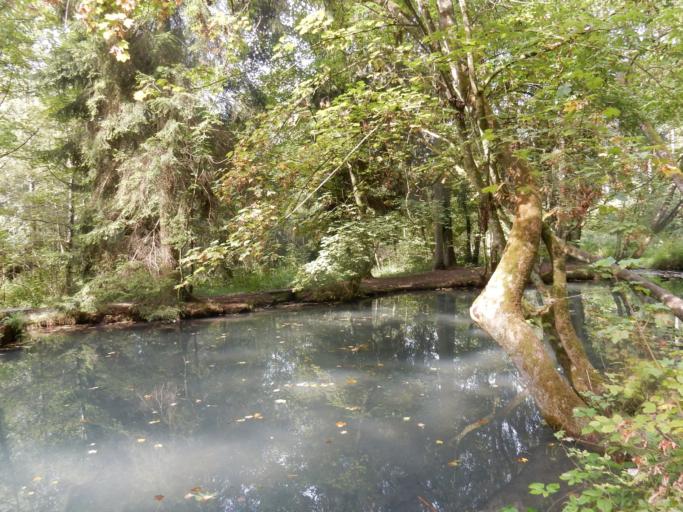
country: LU
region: Luxembourg
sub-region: Canton de Mersch
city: Mersch
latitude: 49.7260
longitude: 6.0868
